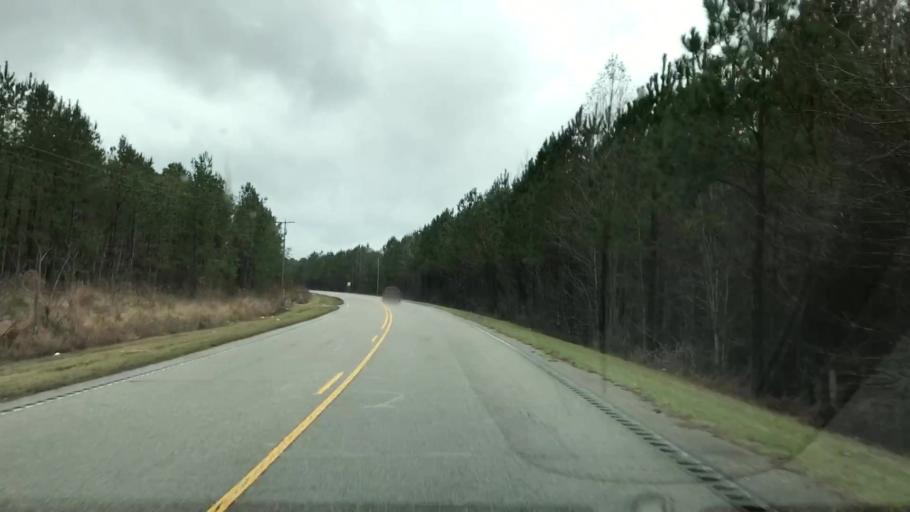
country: US
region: South Carolina
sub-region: Williamsburg County
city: Andrews
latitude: 33.5369
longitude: -79.4832
